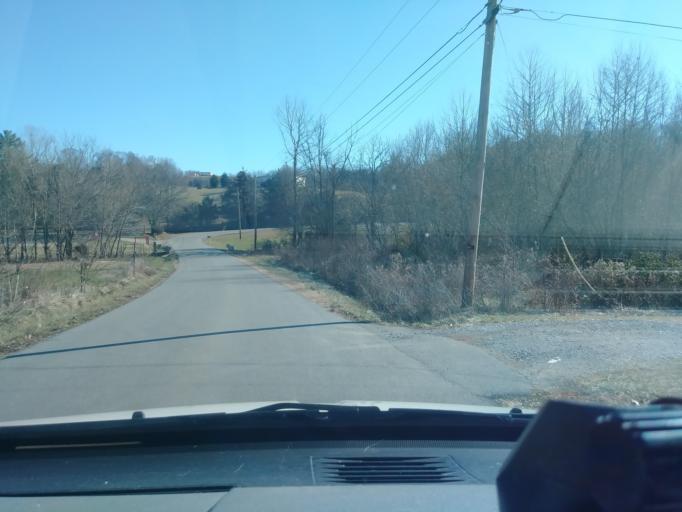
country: US
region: Tennessee
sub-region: Greene County
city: Mosheim
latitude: 36.1055
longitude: -82.9108
